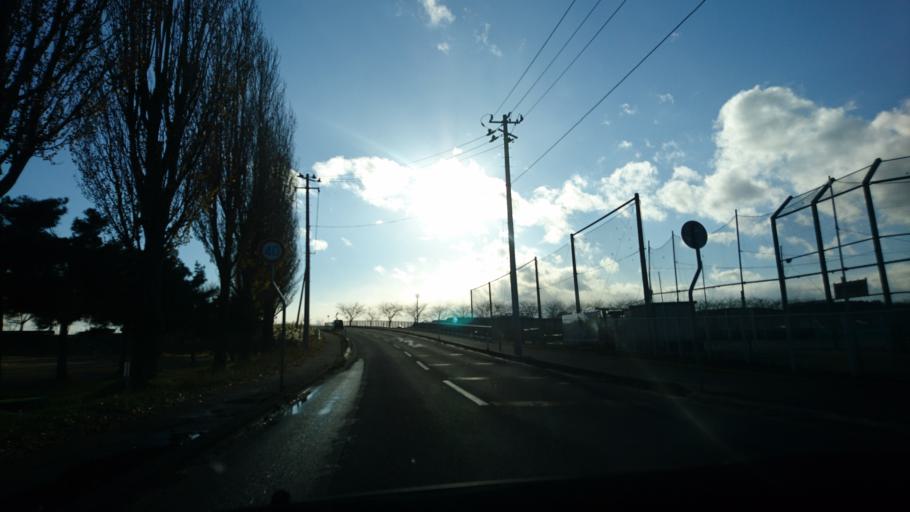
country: JP
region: Iwate
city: Mizusawa
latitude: 39.0573
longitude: 141.1393
